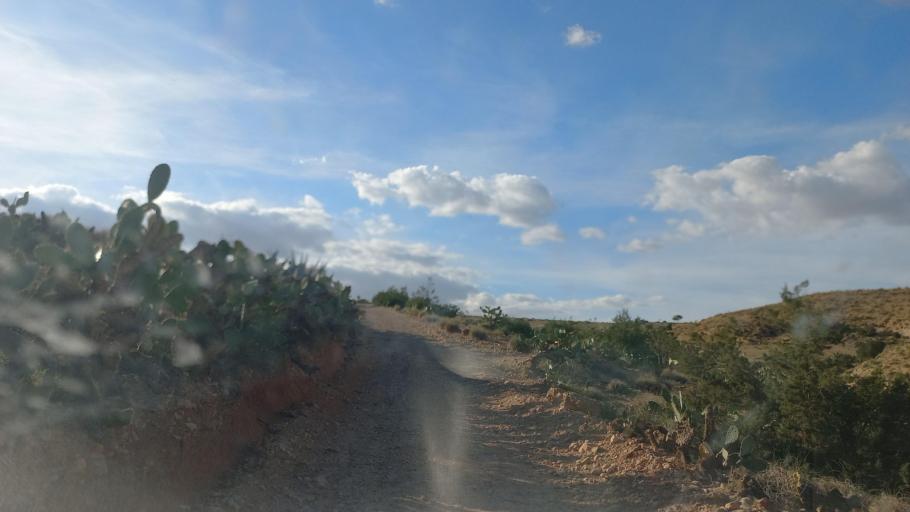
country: TN
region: Al Qasrayn
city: Sbiba
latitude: 35.3824
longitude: 9.0196
